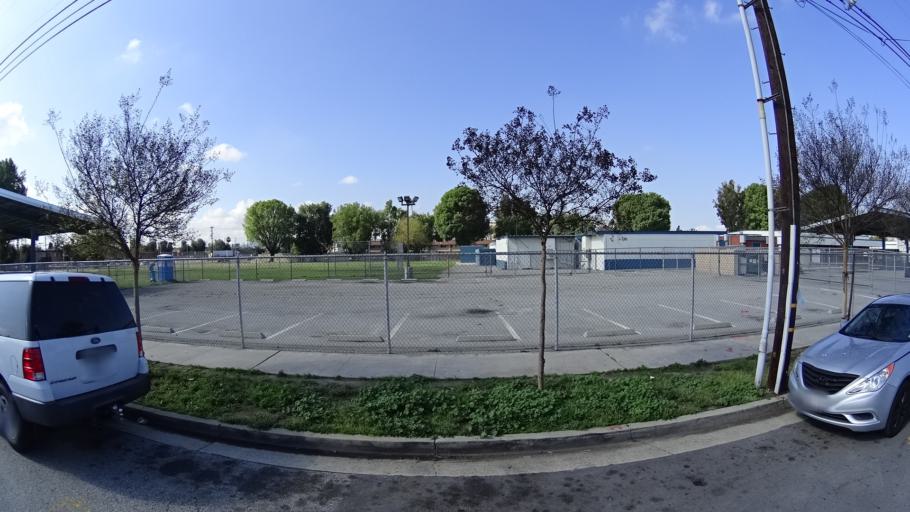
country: US
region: California
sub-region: Los Angeles County
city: Baldwin Park
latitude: 34.0713
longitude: -117.9709
